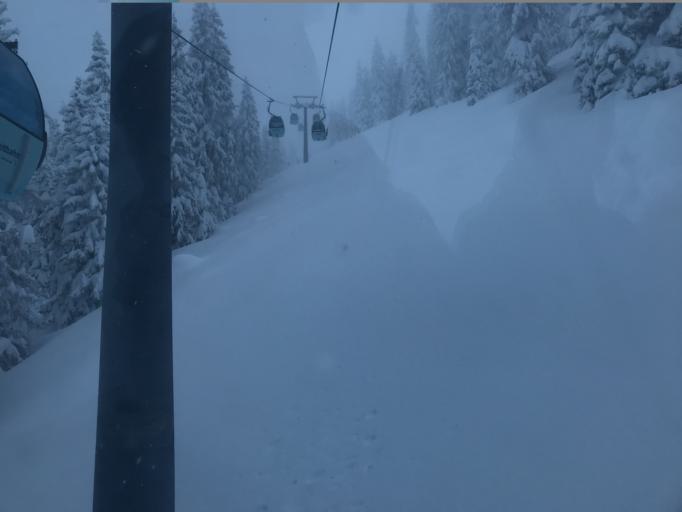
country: AT
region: Salzburg
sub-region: Politischer Bezirk Zell am See
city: Piesendorf
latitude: 47.3210
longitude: 12.7410
